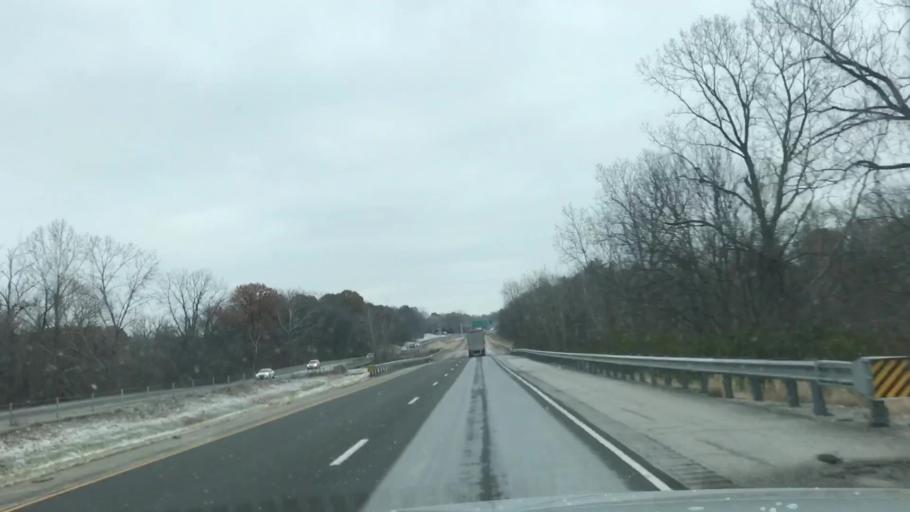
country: US
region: Illinois
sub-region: Madison County
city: Glen Carbon
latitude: 38.7568
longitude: -89.9685
